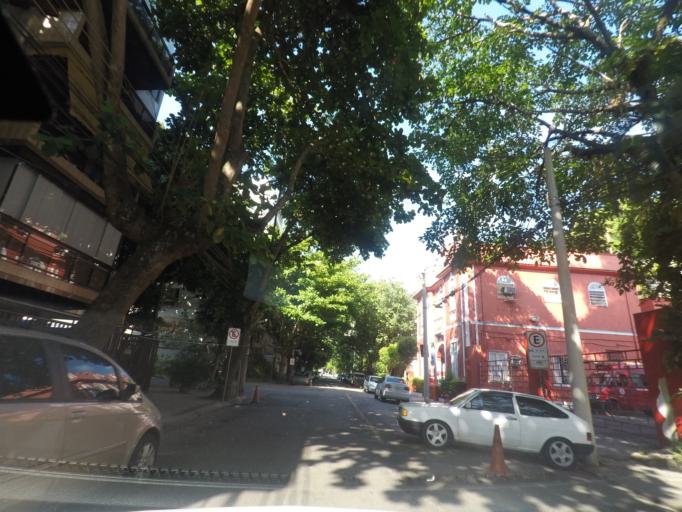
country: BR
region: Rio de Janeiro
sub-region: Rio De Janeiro
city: Rio de Janeiro
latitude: -22.9725
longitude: -43.2257
